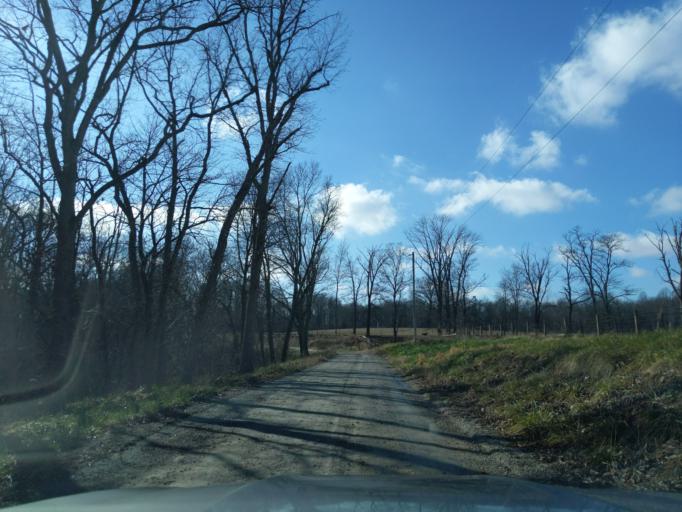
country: US
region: Indiana
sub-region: Decatur County
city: Greensburg
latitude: 39.2440
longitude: -85.4717
